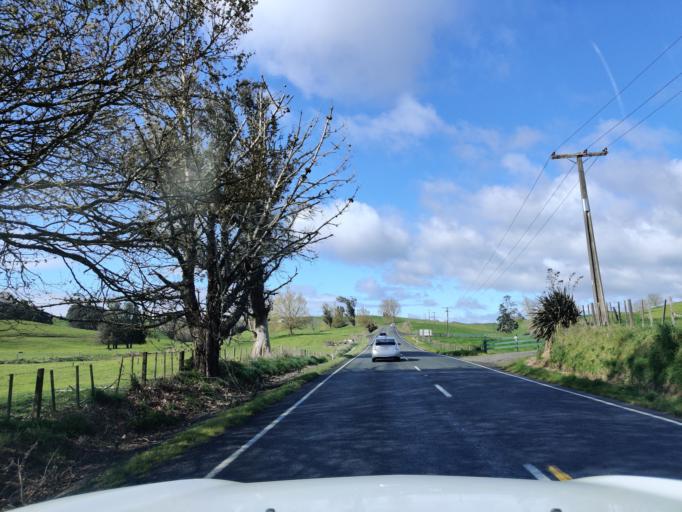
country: NZ
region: Waikato
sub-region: Otorohanga District
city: Otorohanga
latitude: -38.0894
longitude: 175.1821
